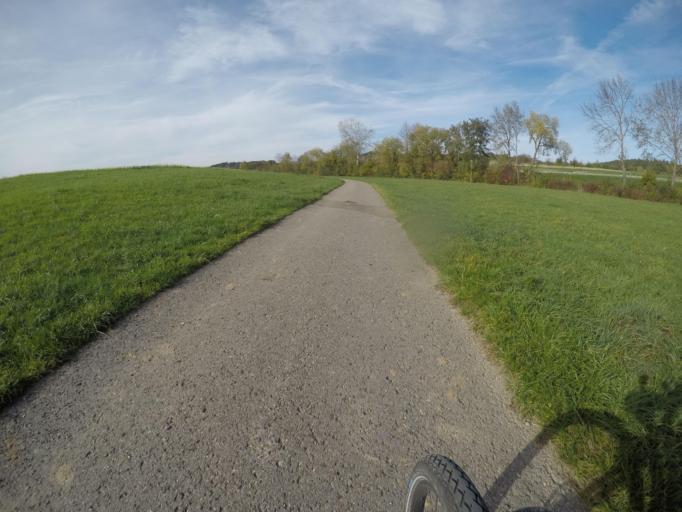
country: DE
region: Baden-Wuerttemberg
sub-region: Karlsruhe Region
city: Simmozheim
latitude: 48.7481
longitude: 8.8281
